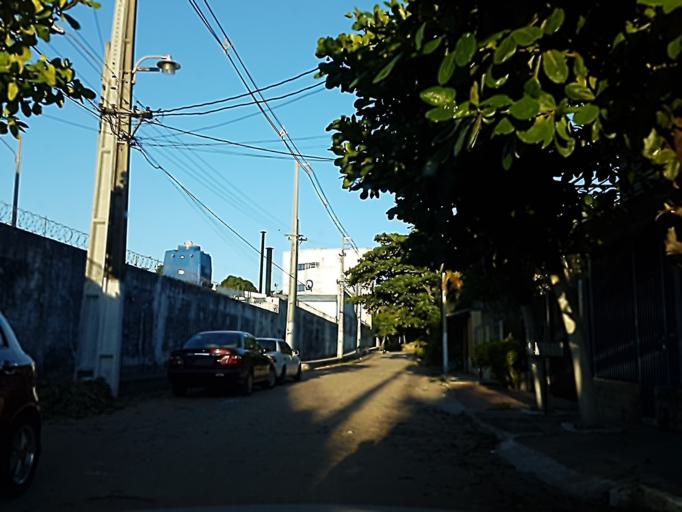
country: PY
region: Asuncion
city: Asuncion
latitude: -25.2574
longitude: -57.5731
